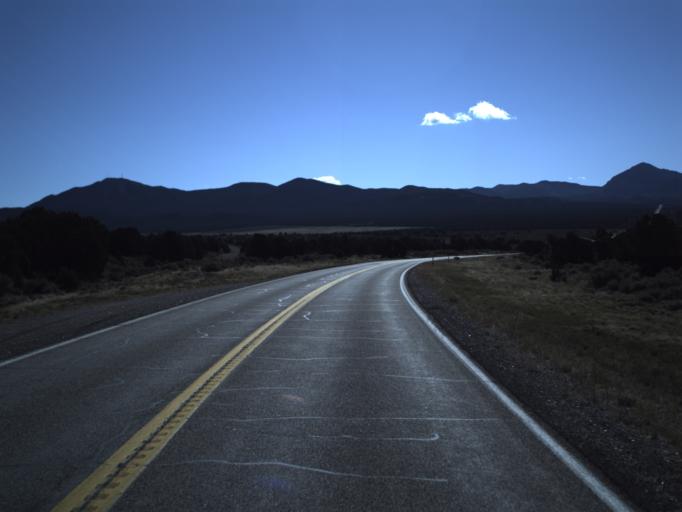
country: US
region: Utah
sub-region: Washington County
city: Enterprise
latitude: 37.6619
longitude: -113.4634
